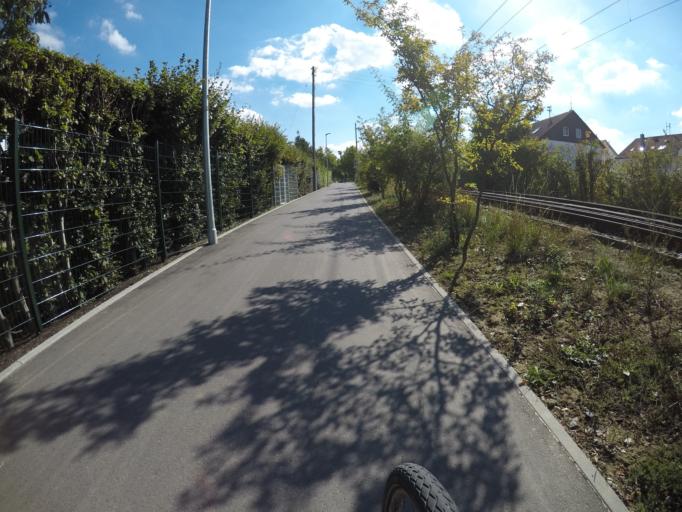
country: DE
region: Baden-Wuerttemberg
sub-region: Regierungsbezirk Stuttgart
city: Leinfelden-Echterdingen
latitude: 48.7060
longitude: 9.1434
